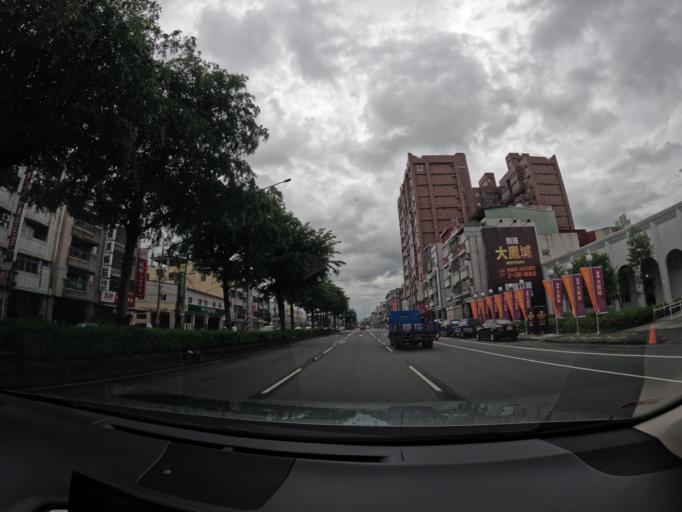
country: TW
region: Taiwan
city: Fengshan
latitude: 22.6268
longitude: 120.3772
